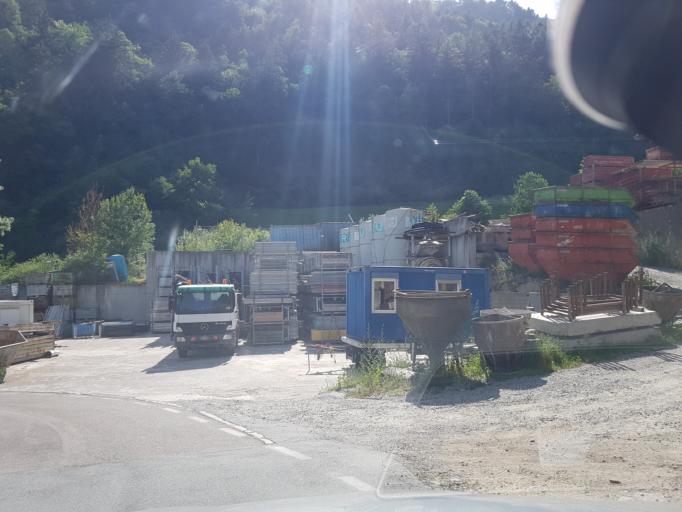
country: IT
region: Trentino-Alto Adige
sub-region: Bolzano
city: Villandro - Villanders
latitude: 46.6171
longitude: 11.5329
